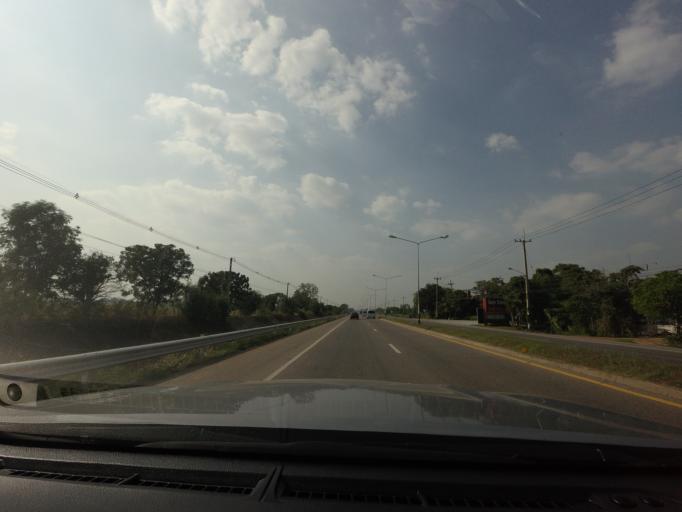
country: TH
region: Sukhothai
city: Sukhothai
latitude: 17.0169
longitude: 99.9078
